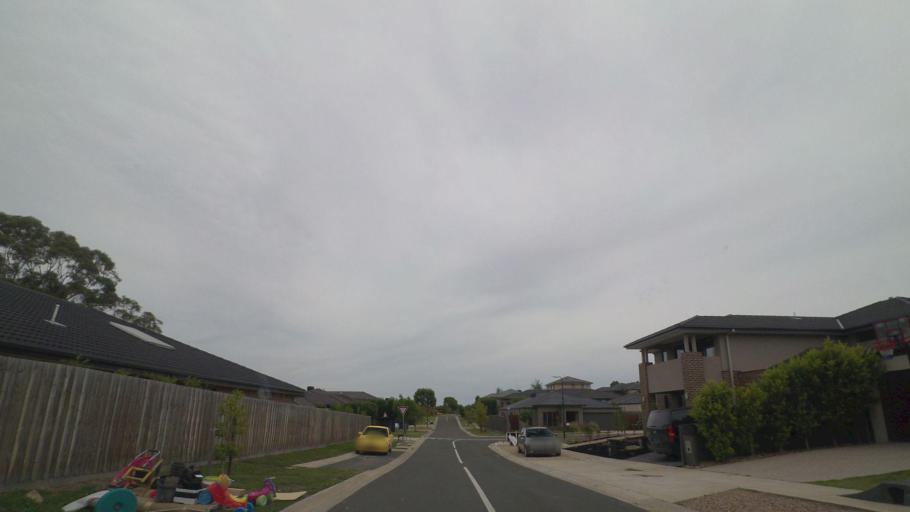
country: AU
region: Victoria
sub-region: Yarra Ranges
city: Lilydale
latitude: -37.7778
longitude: 145.3435
